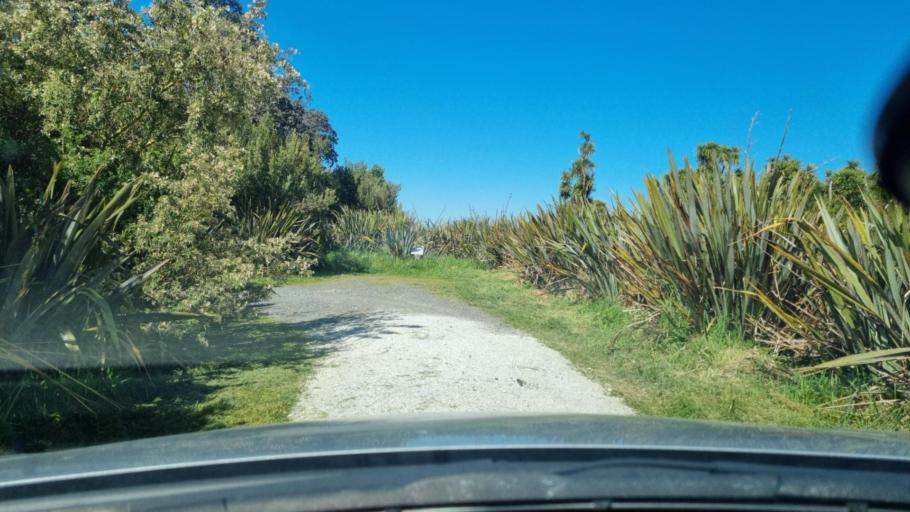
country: NZ
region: Southland
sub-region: Invercargill City
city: Invercargill
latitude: -46.4530
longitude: 168.3166
